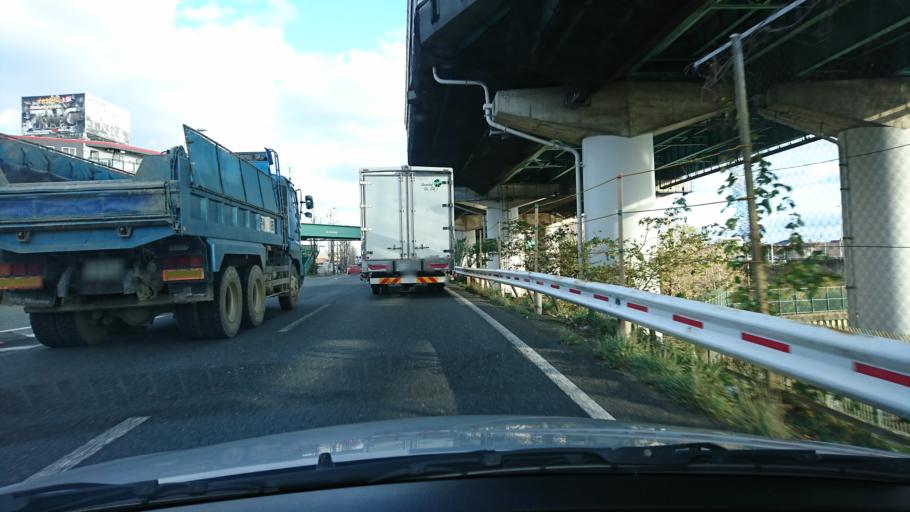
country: JP
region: Osaka
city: Ikeda
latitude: 34.8008
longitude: 135.4402
